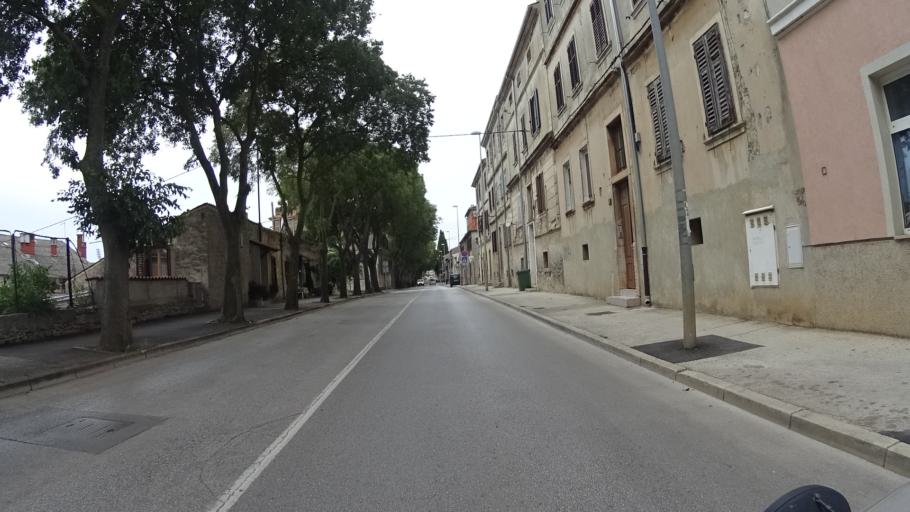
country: HR
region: Istarska
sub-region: Grad Pula
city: Pula
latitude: 44.8635
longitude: 13.8573
